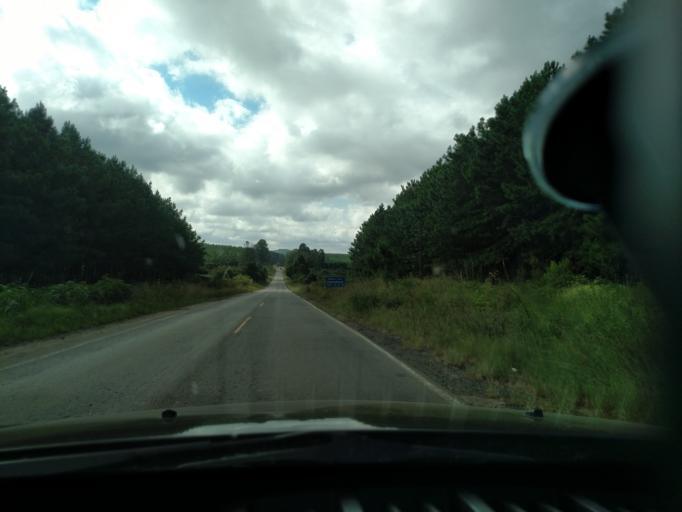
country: BR
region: Santa Catarina
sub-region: Lages
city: Lages
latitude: -27.8305
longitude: -50.2453
